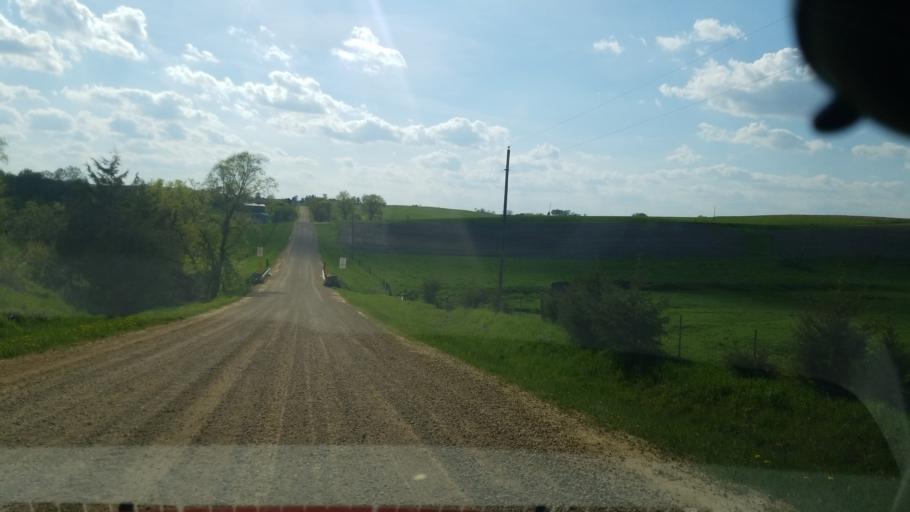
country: US
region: Iowa
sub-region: Jackson County
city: Maquoketa
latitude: 42.2149
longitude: -90.6907
